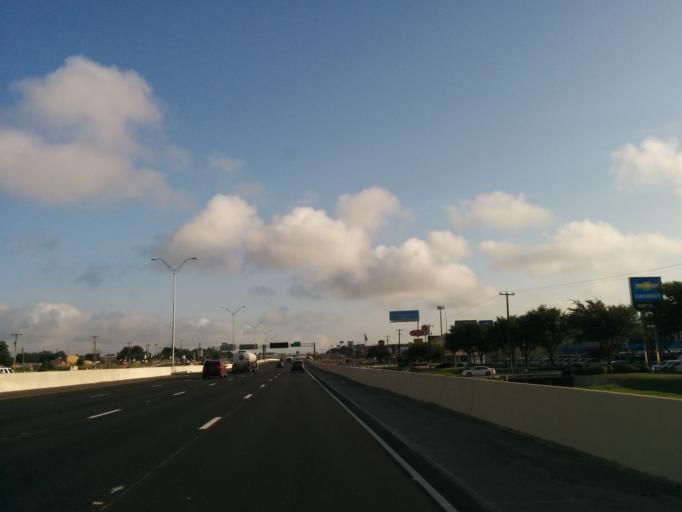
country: US
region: Texas
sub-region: Bexar County
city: Shavano Park
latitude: 29.5680
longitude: -98.5924
